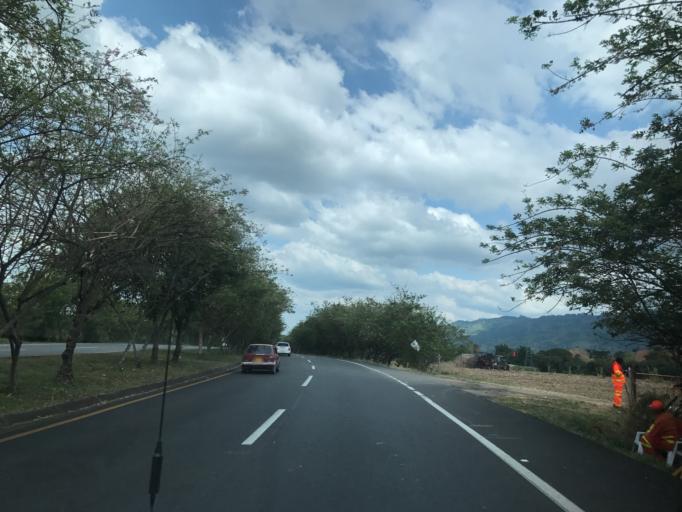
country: CO
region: Valle del Cauca
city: Obando
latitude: 4.6191
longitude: -75.9429
